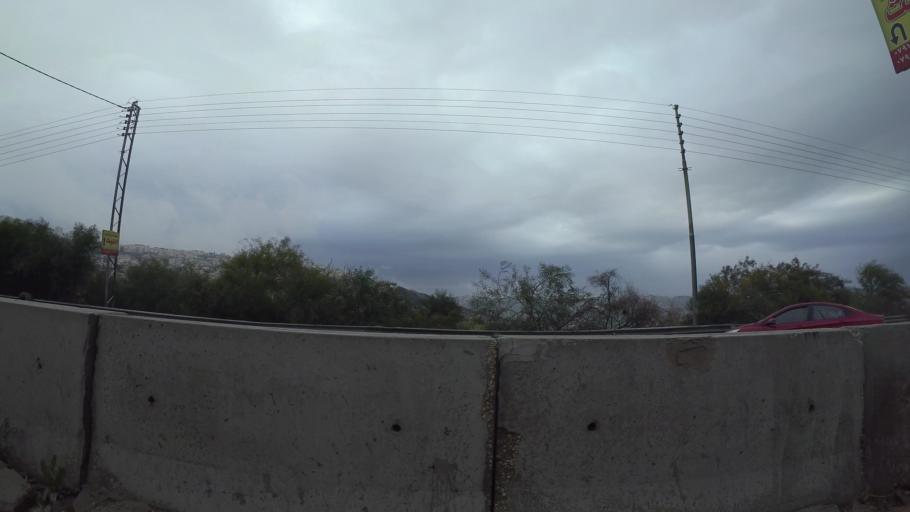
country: JO
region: Amman
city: Al Jubayhah
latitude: 32.0427
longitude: 35.8367
